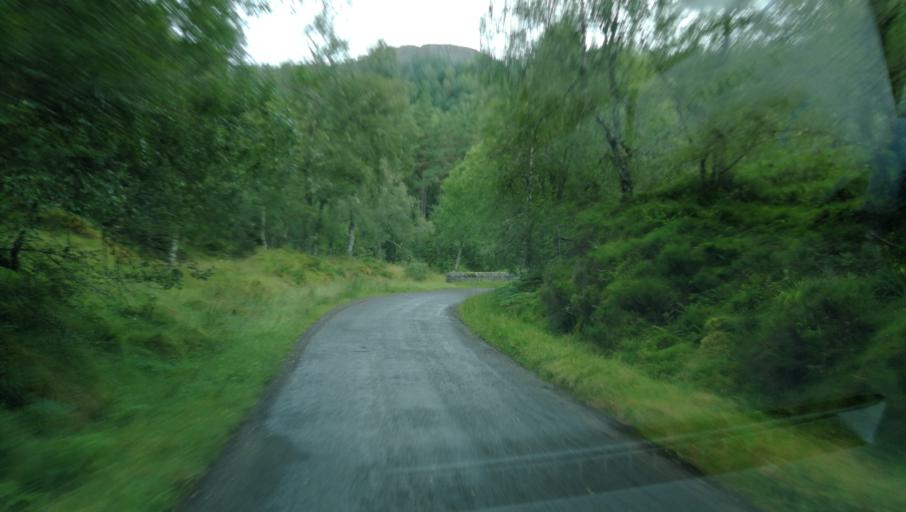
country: GB
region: Scotland
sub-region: Highland
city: Spean Bridge
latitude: 57.3043
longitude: -4.8744
